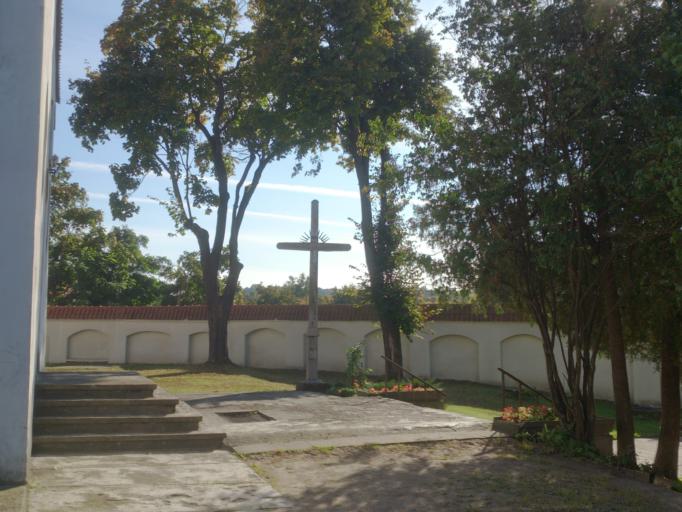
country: LT
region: Kauno apskritis
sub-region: Kaunas
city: Kaunas
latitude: 54.8994
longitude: 23.8935
